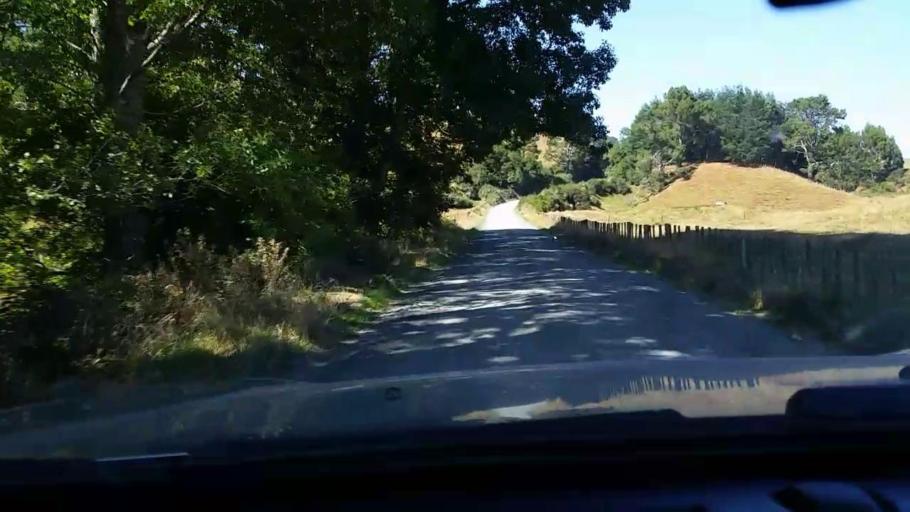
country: NZ
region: Bay of Plenty
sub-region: Rotorua District
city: Rotorua
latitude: -38.3814
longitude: 176.2016
